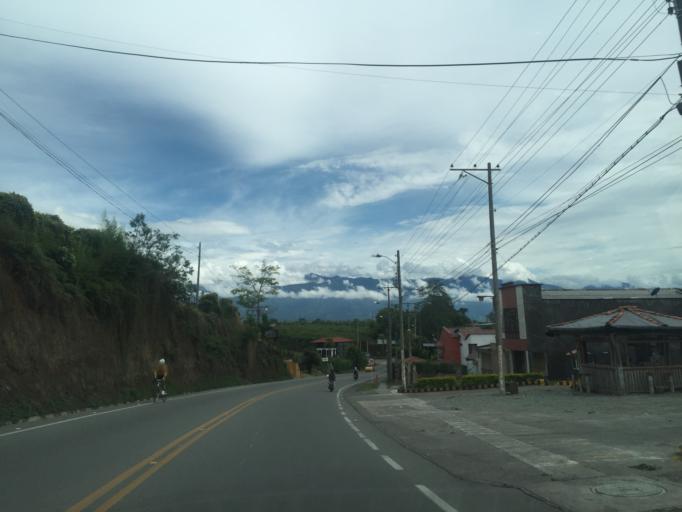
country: CO
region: Quindio
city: Montenegro
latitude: 4.5605
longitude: -75.7496
